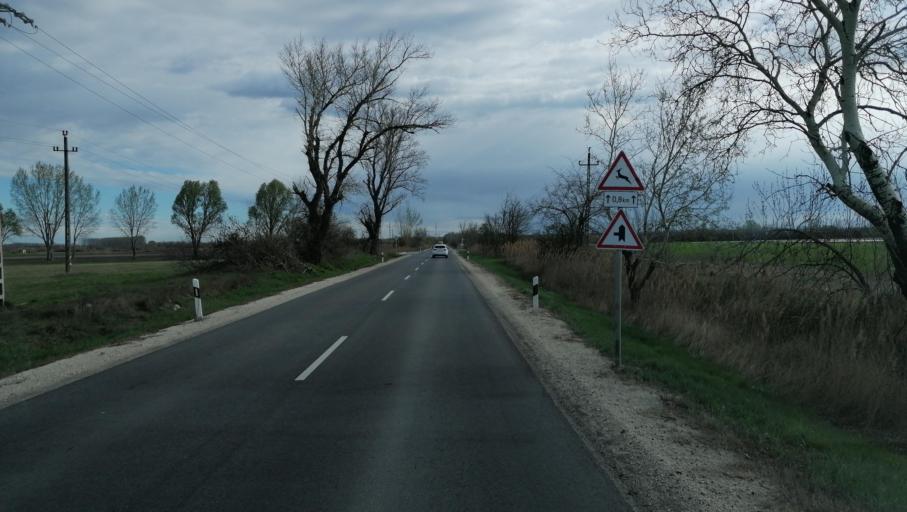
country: HU
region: Pest
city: Ocsa
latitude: 47.2484
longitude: 19.2031
